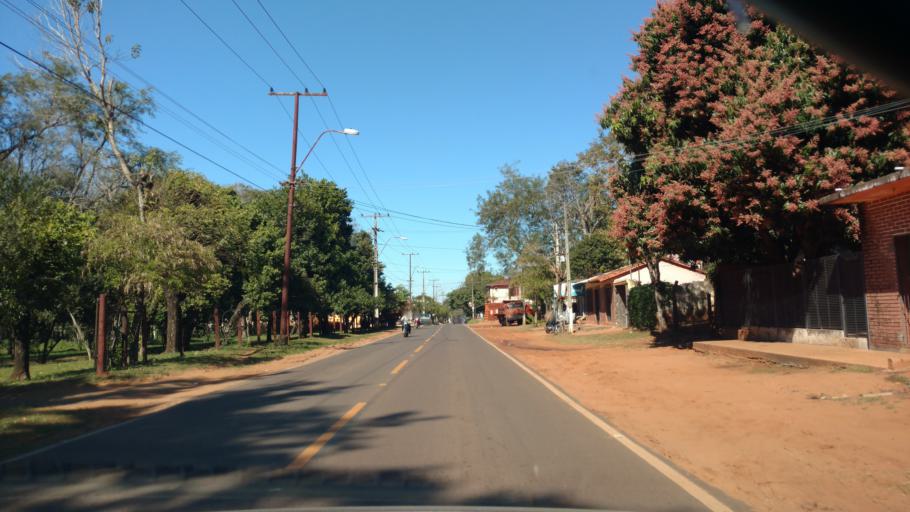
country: PY
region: Paraguari
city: Yaguaron
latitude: -25.5551
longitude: -57.2832
